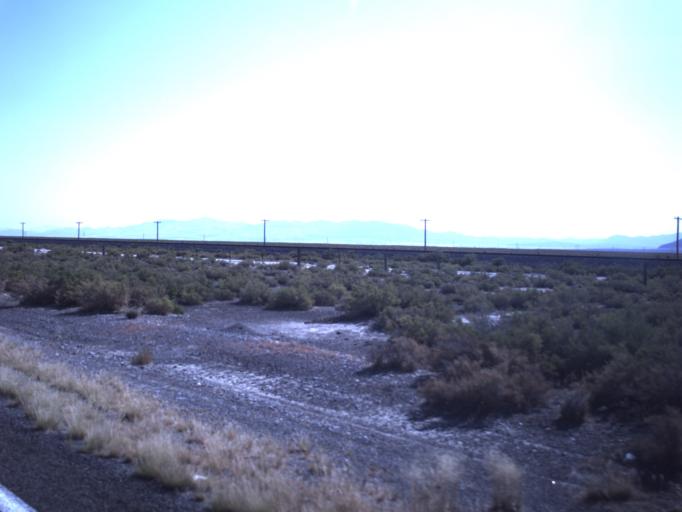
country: US
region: Utah
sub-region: Millard County
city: Delta
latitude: 39.1227
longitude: -112.7368
